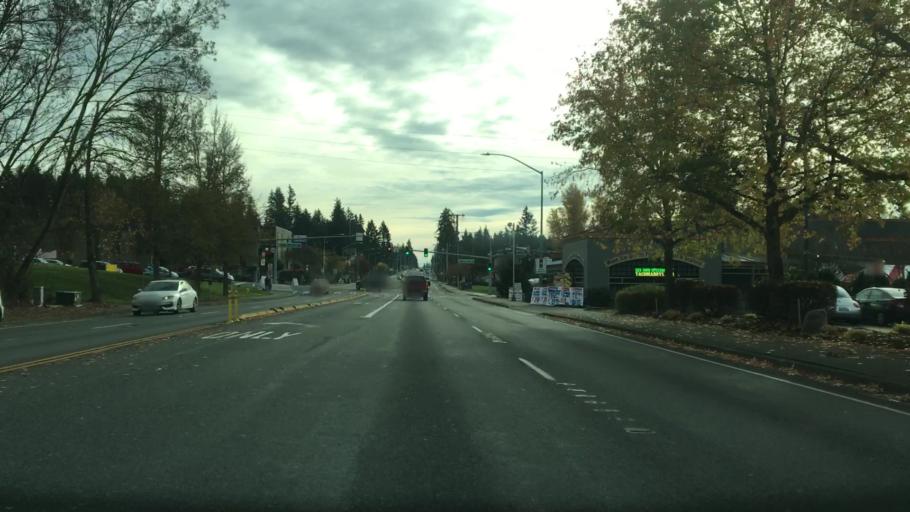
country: US
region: Washington
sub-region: Pierce County
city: Puyallup
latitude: 47.1559
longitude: -122.3040
